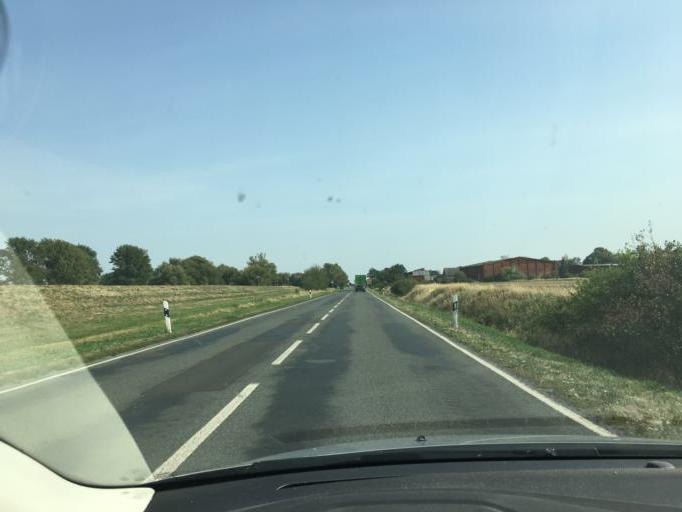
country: DE
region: Saxony-Anhalt
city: Plotzky
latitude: 52.0082
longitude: 11.7957
